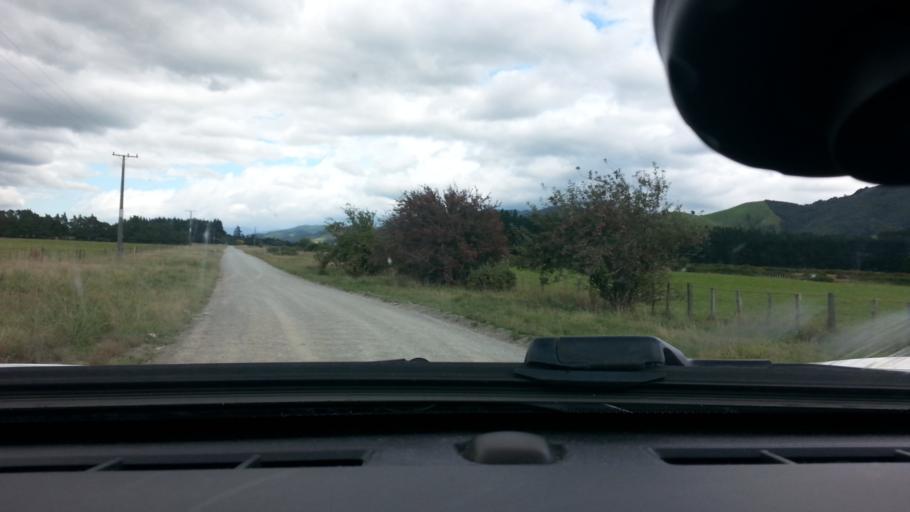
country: NZ
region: Wellington
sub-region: Masterton District
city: Masterton
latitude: -41.0639
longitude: 175.4003
